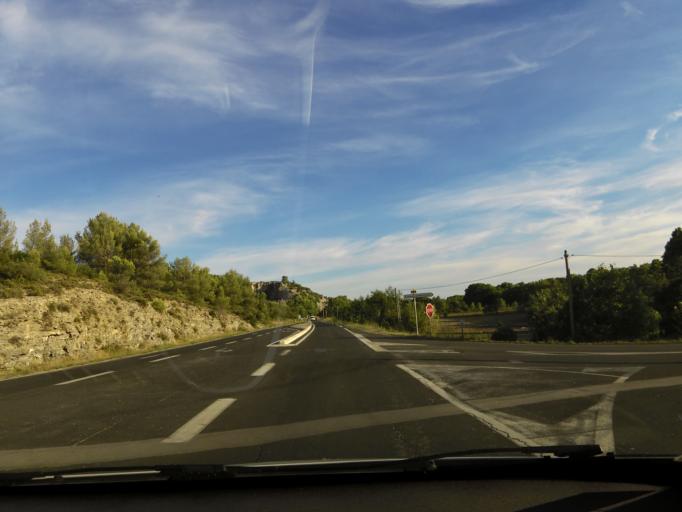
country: FR
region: Languedoc-Roussillon
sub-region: Departement de l'Herault
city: Prades-le-Lez
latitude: 43.7127
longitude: 3.8668
